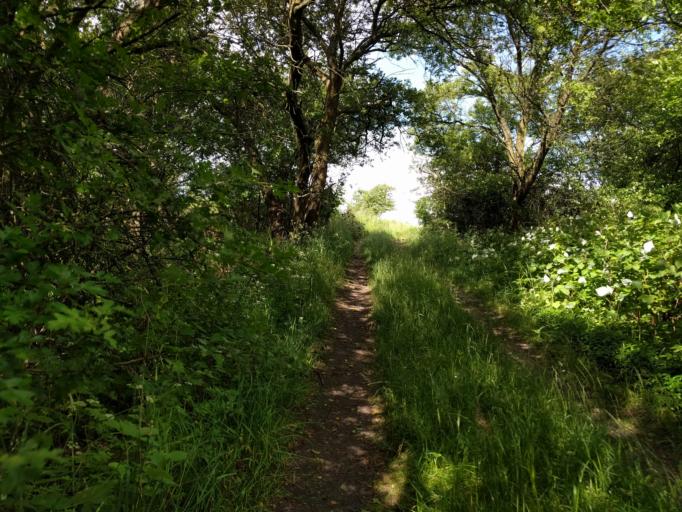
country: DK
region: South Denmark
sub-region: Kerteminde Kommune
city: Munkebo
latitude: 55.4669
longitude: 10.5118
